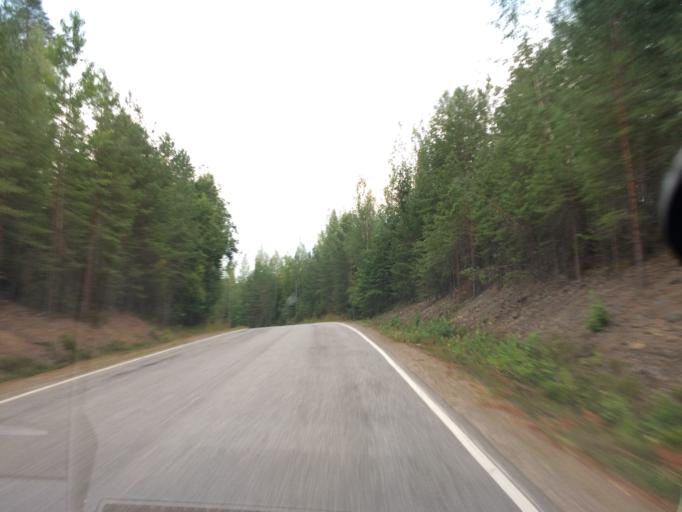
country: FI
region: Haeme
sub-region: Haemeenlinna
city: Tuulos
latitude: 61.2286
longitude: 24.7097
